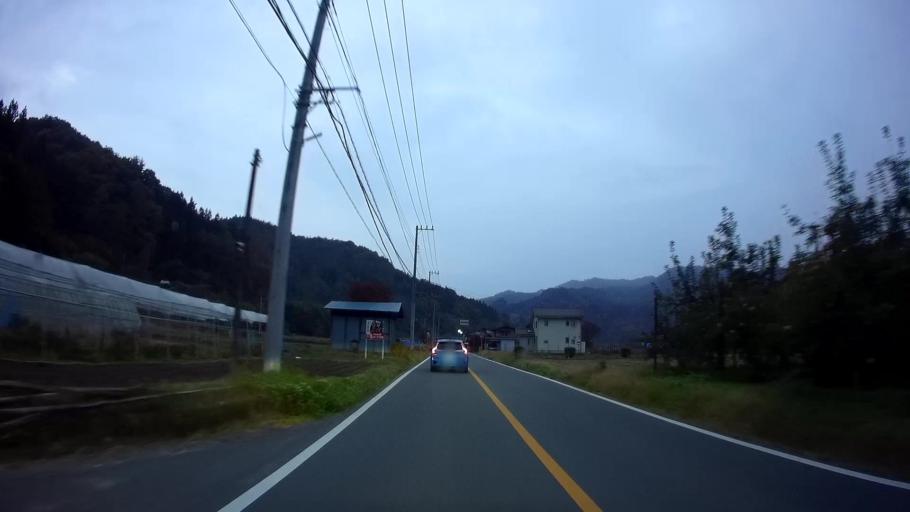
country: JP
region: Gunma
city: Nakanojomachi
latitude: 36.5351
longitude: 138.7852
